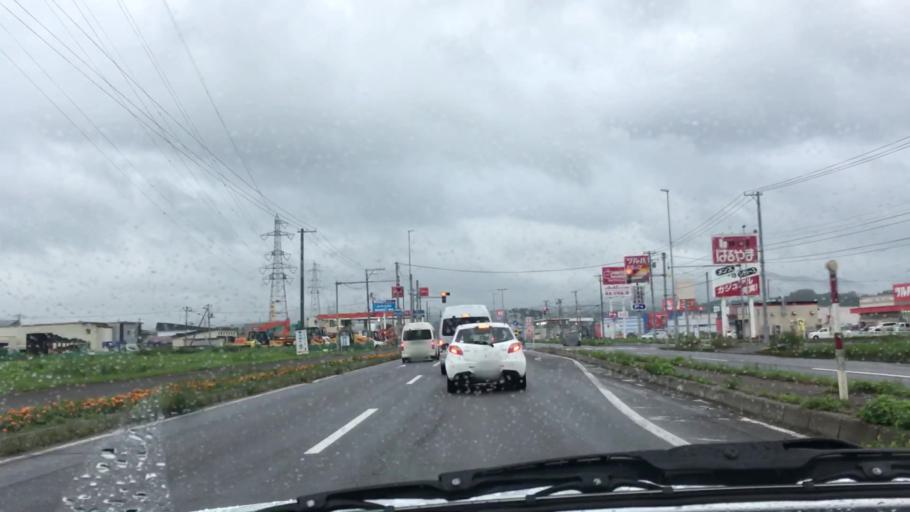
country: JP
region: Hokkaido
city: Nanae
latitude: 42.2528
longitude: 140.2841
